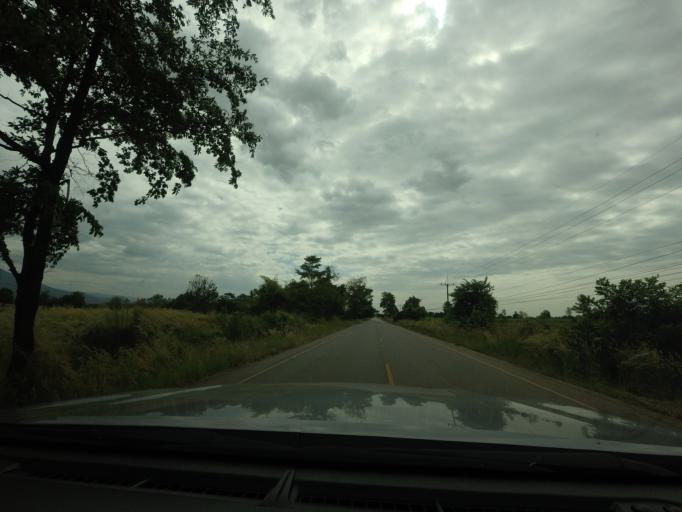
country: TH
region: Phitsanulok
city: Noen Maprang
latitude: 16.6564
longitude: 100.6157
